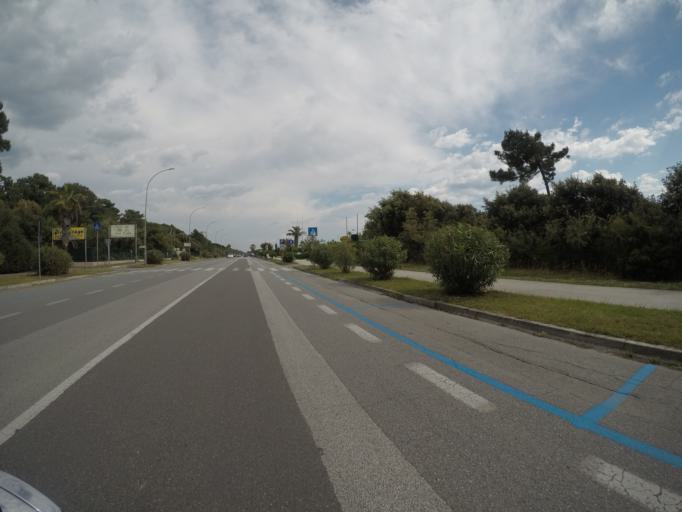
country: IT
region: Tuscany
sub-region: Provincia di Massa-Carrara
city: Massa
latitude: 43.9924
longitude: 10.1235
